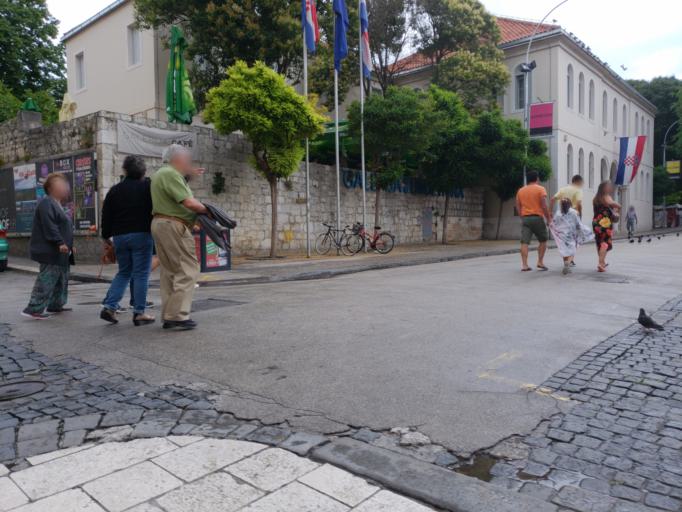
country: HR
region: Splitsko-Dalmatinska
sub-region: Grad Split
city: Split
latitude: 43.5097
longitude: 16.4398
